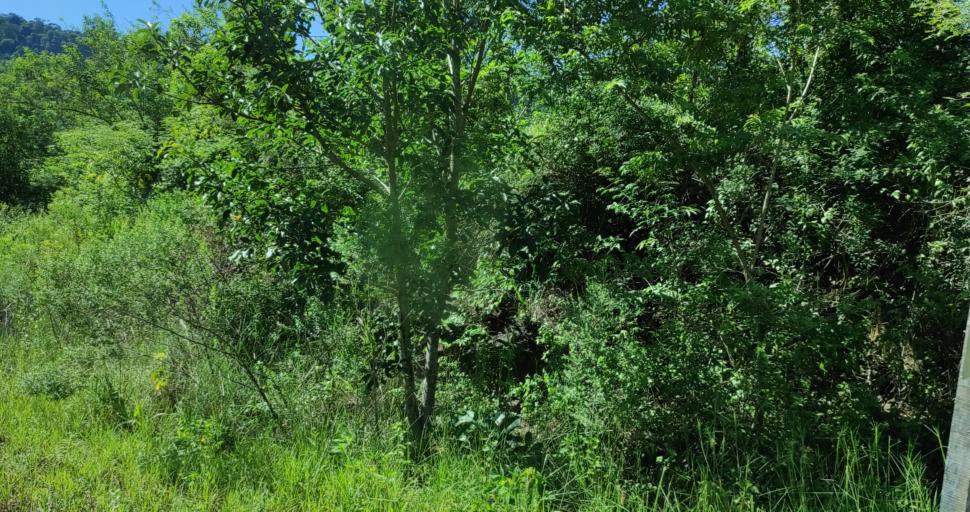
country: BR
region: Rio Grande do Sul
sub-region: Tres Passos
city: Tres Passos
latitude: -27.1459
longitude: -53.9108
